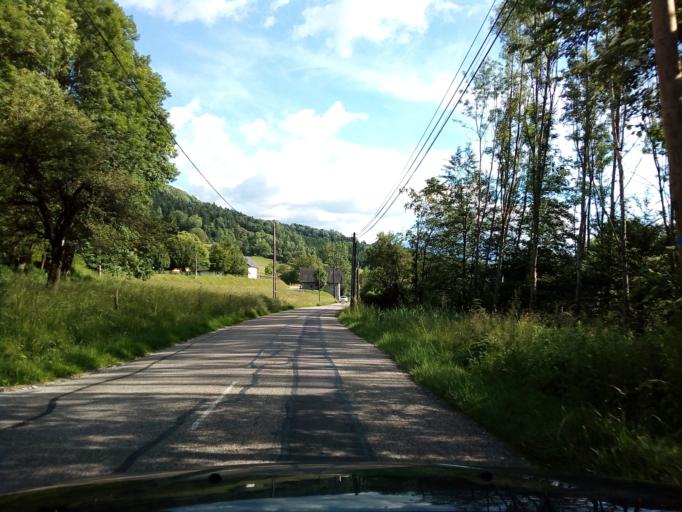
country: FR
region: Rhone-Alpes
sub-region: Departement de la Savoie
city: Saint-Beron
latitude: 45.4773
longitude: 5.7627
